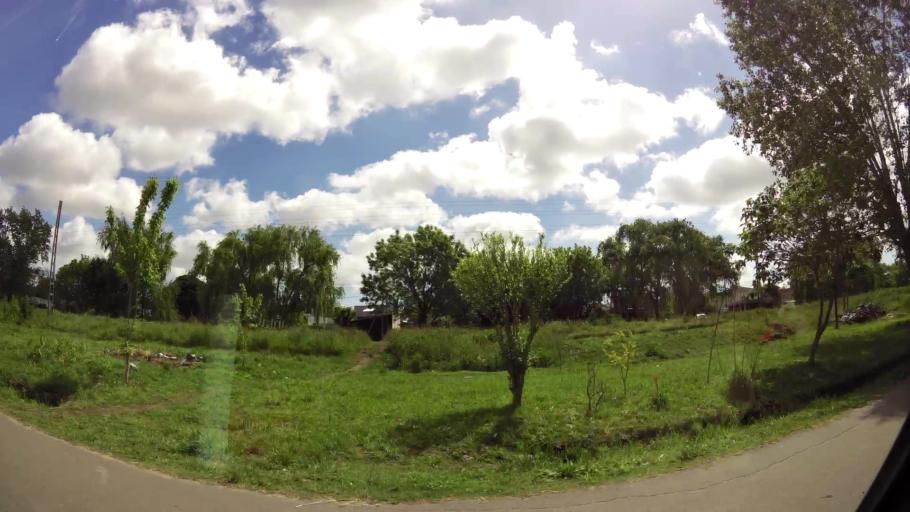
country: AR
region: Buenos Aires
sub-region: Partido de Quilmes
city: Quilmes
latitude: -34.8364
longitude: -58.1789
